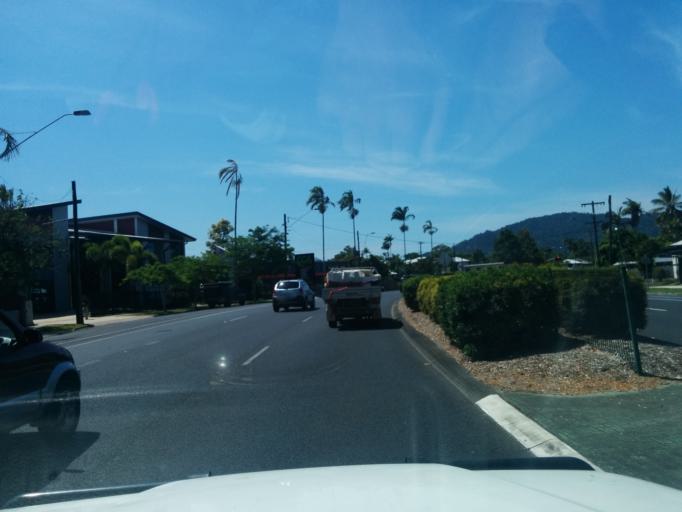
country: AU
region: Queensland
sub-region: Cairns
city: Cairns
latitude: -16.9244
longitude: 145.7404
